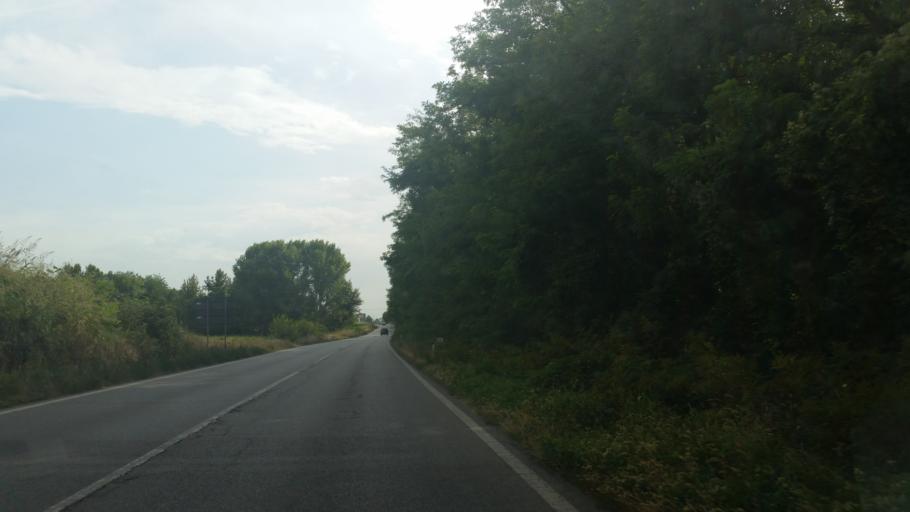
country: IT
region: Lombardy
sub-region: Provincia di Brescia
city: San Paolo
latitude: 45.3704
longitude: 10.0509
